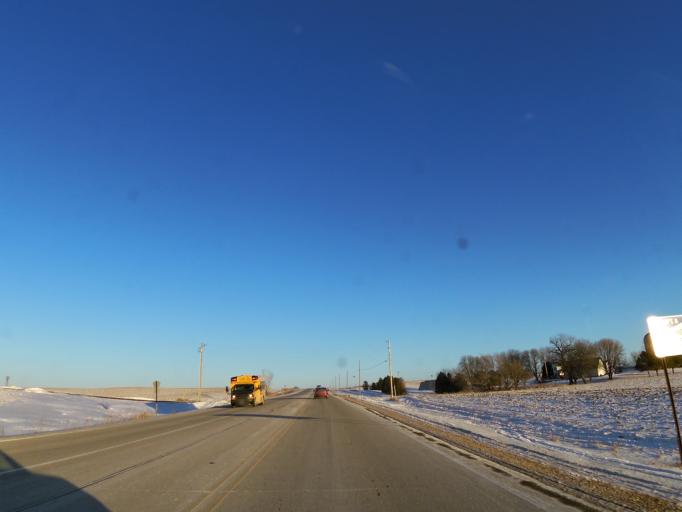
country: US
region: Minnesota
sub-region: Scott County
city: Shakopee
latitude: 44.7616
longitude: -93.5605
